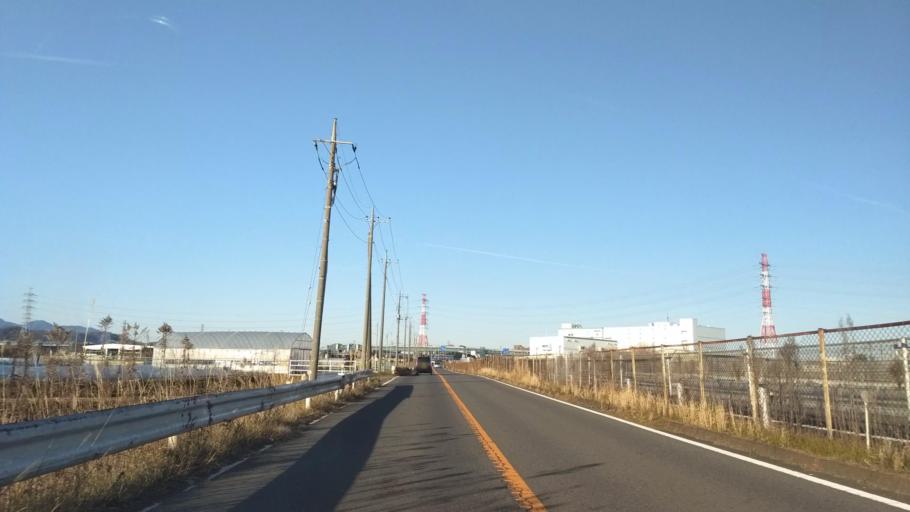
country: JP
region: Kanagawa
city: Isehara
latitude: 35.3993
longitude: 139.3348
